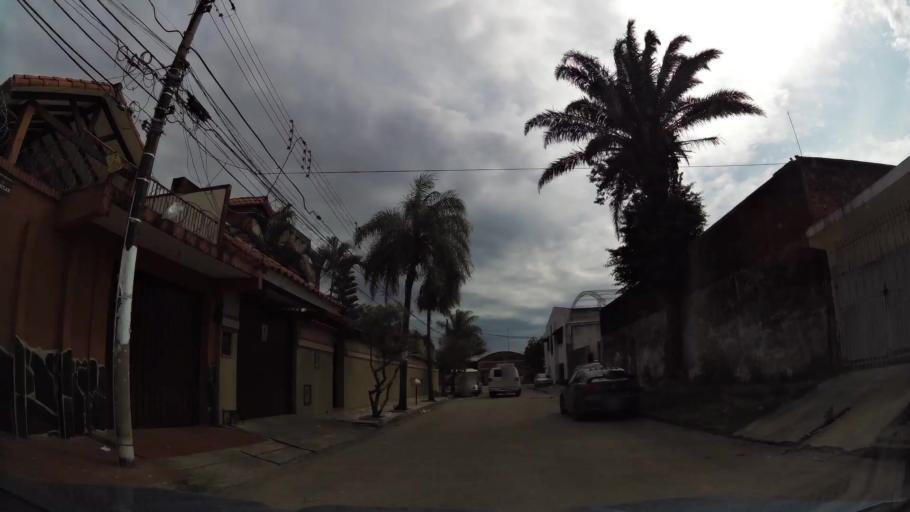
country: BO
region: Santa Cruz
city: Santa Cruz de la Sierra
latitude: -17.7859
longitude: -63.2002
